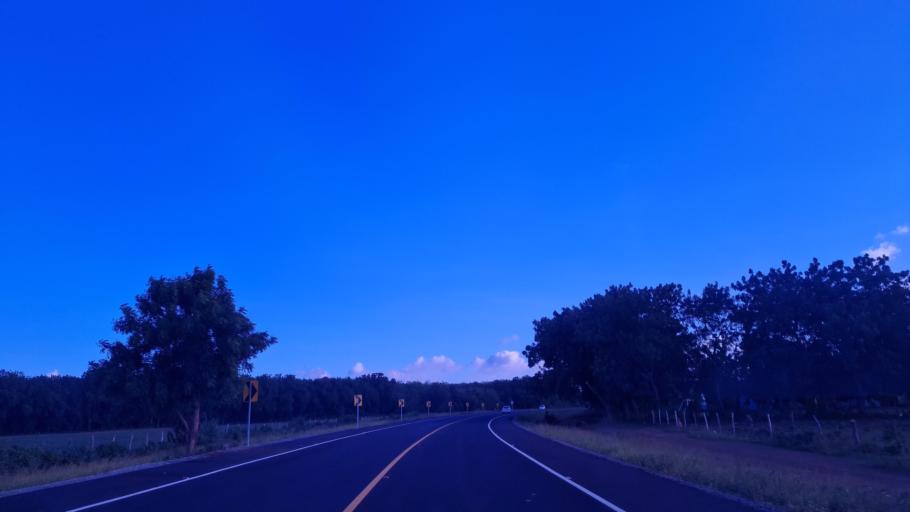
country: NI
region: Masaya
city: Ticuantepe
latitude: 12.0974
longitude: -86.1594
